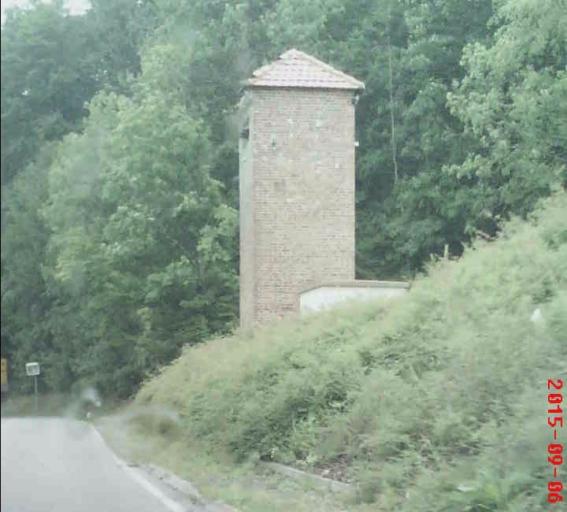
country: DE
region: Thuringia
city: Brehme
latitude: 51.4972
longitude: 10.3807
